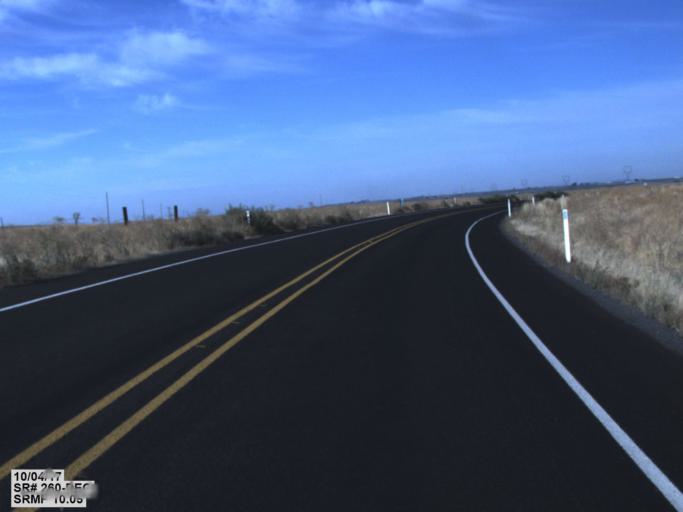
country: US
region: Washington
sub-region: Franklin County
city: Connell
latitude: 46.6348
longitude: -118.8076
